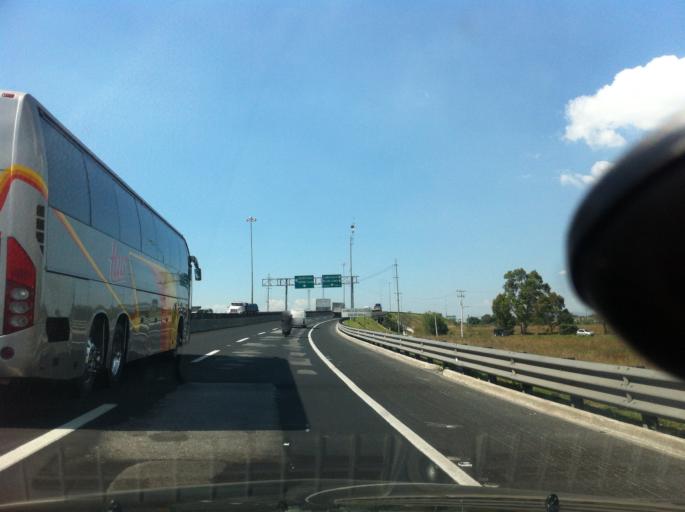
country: MX
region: Mexico
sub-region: Cuautitlan
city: La Providencia
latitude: 19.7495
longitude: -99.1256
